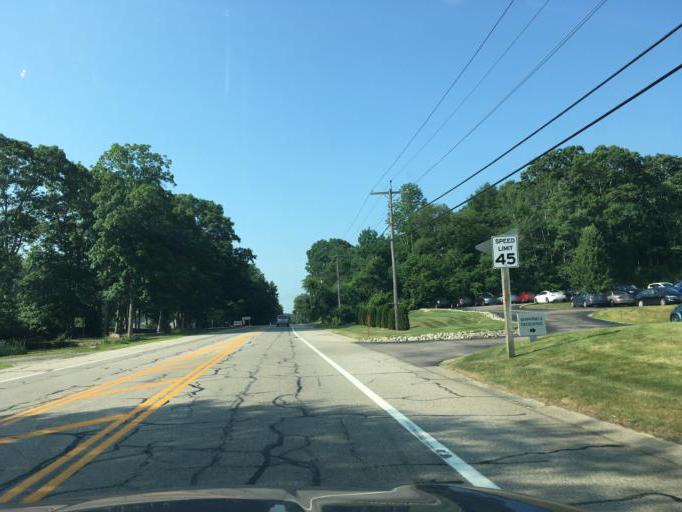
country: US
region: Rhode Island
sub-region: Washington County
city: Kingston
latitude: 41.5213
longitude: -71.5540
